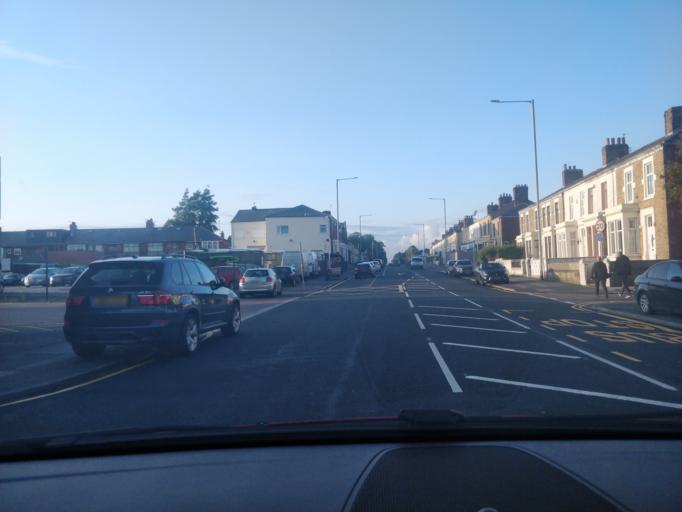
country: GB
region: England
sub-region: Lancashire
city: Preston
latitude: 53.7683
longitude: -2.6914
